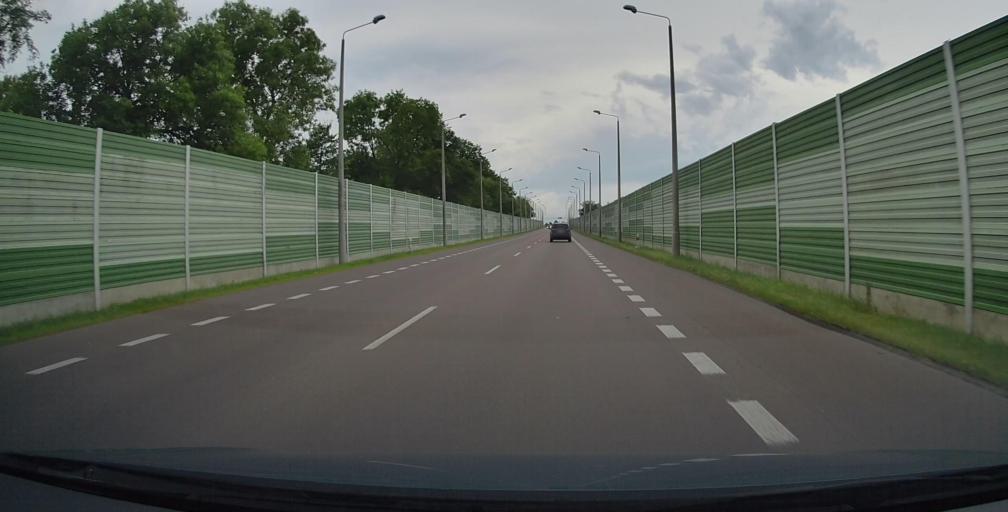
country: PL
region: Lublin Voivodeship
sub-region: Biala Podlaska
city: Biala Podlaska
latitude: 52.0403
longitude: 23.1804
